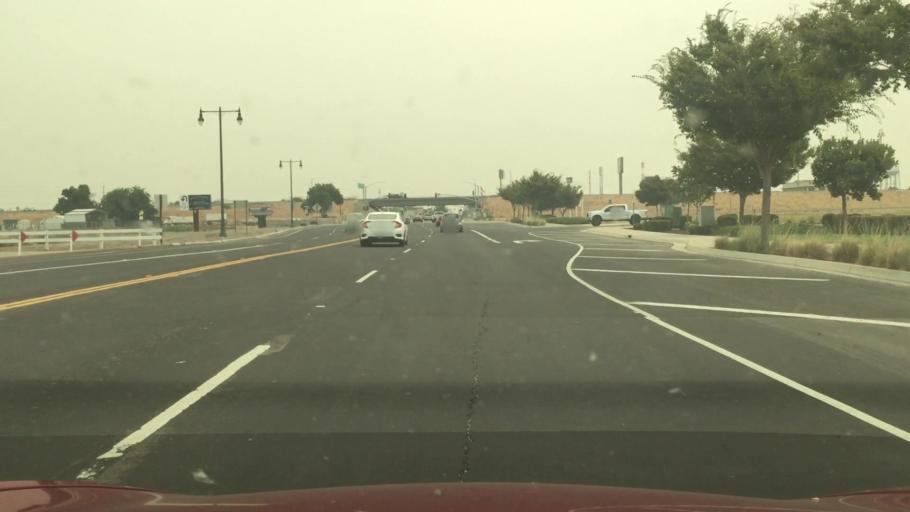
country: US
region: California
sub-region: San Joaquin County
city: Lathrop
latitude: 37.8132
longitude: -121.2992
